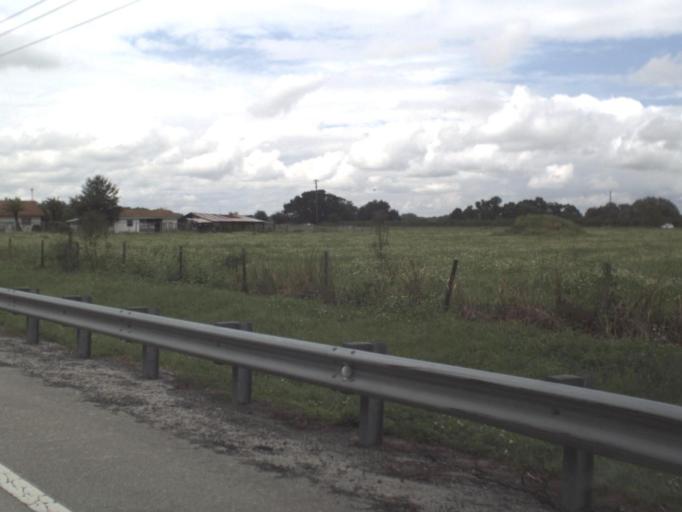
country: US
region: Florida
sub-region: Hardee County
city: Bowling Green
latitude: 27.5948
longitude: -81.9062
